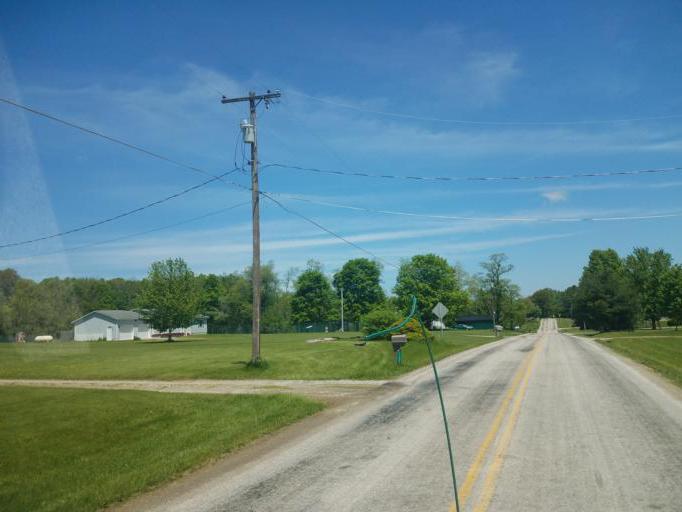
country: US
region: Ohio
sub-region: Ashland County
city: Ashland
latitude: 40.8962
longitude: -82.2494
